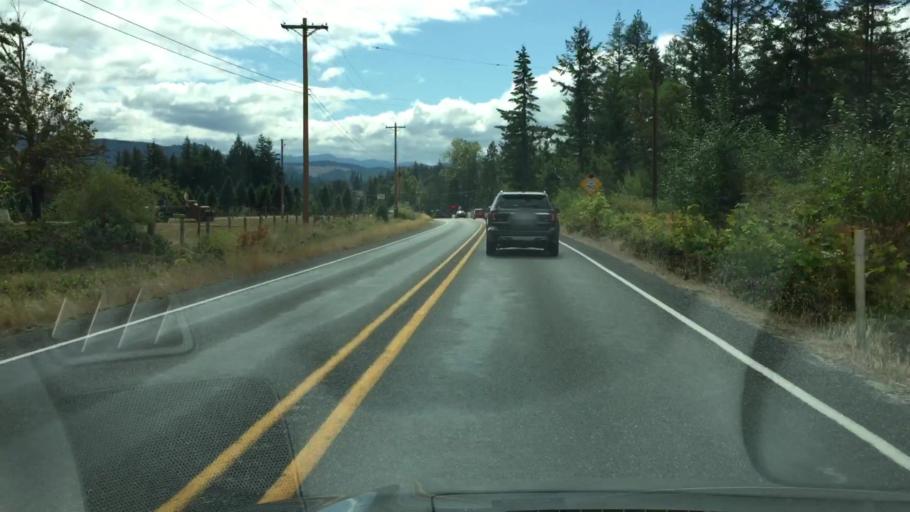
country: US
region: Washington
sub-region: Pierce County
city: Eatonville
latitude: 46.8902
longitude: -122.2994
